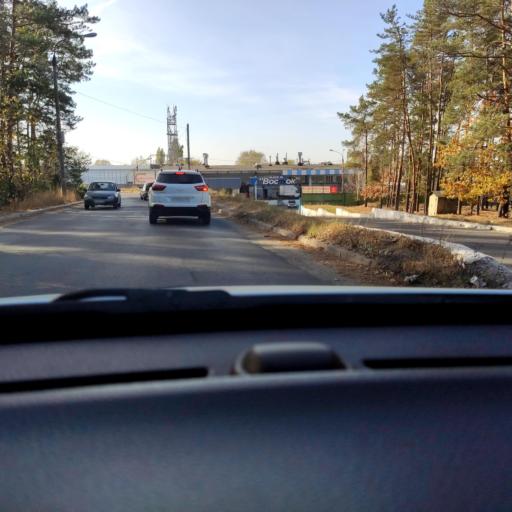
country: RU
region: Voronezj
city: Pridonskoy
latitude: 51.6438
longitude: 39.1091
